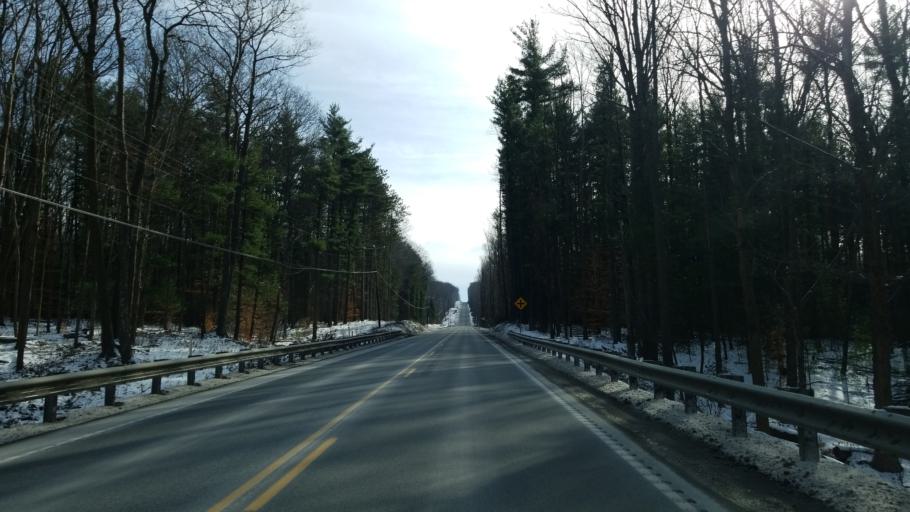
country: US
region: Pennsylvania
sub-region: Clearfield County
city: Clearfield
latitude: 41.1425
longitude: -78.5433
